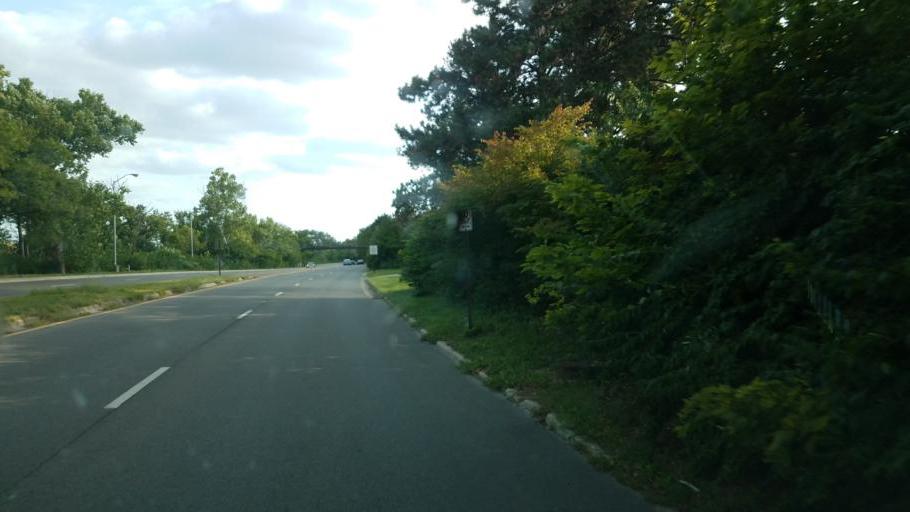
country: US
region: Ohio
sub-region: Franklin County
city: Grandview Heights
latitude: 40.0022
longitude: -83.0241
